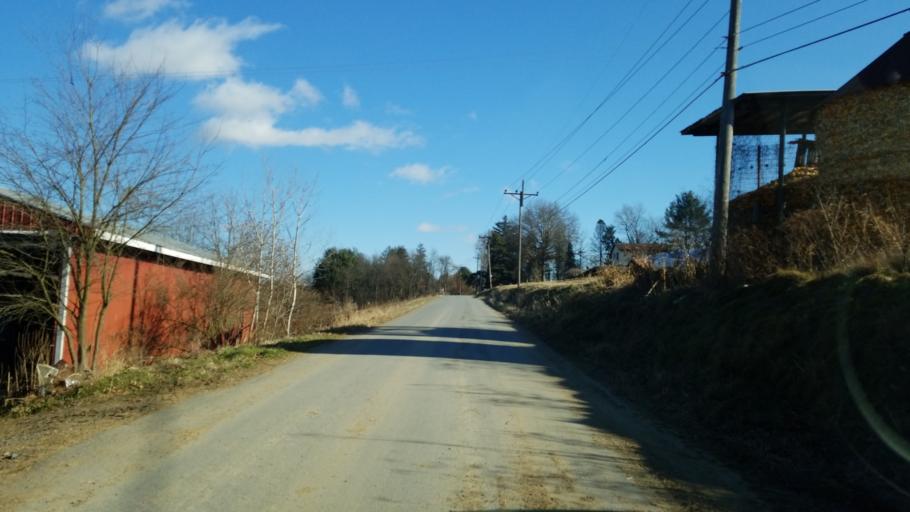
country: US
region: Pennsylvania
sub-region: Clearfield County
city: Curwensville
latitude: 40.9811
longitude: -78.4925
